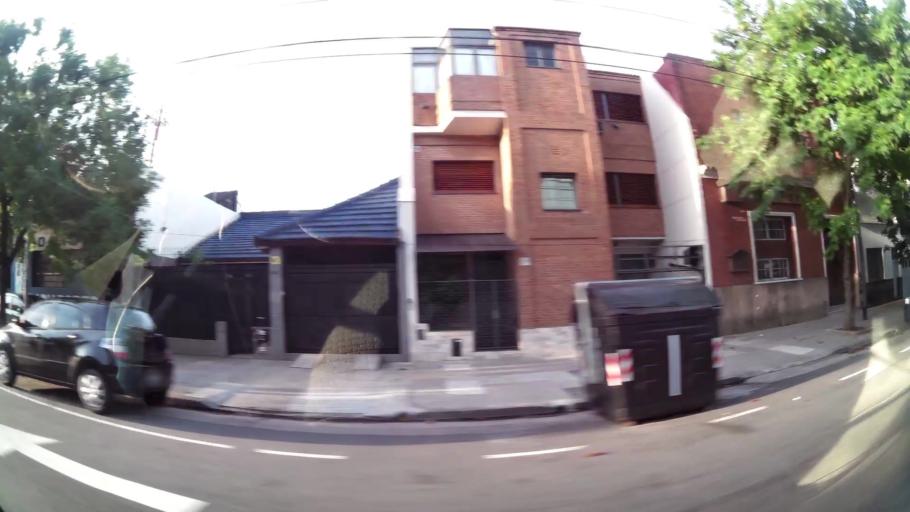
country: AR
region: Buenos Aires F.D.
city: Buenos Aires
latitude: -34.6330
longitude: -58.4291
